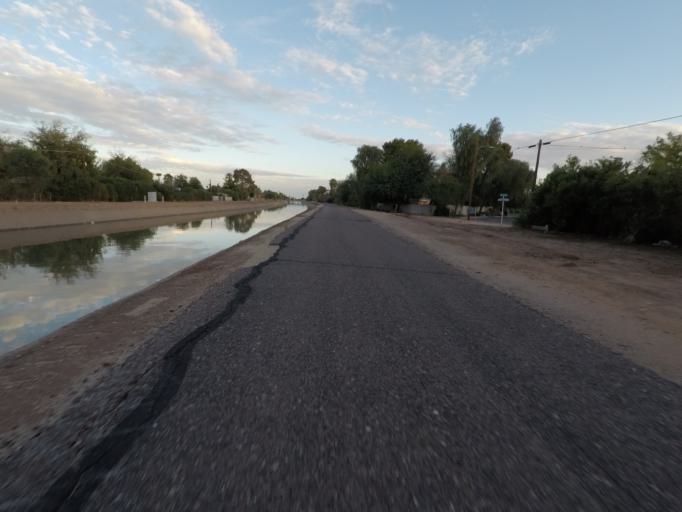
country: US
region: Arizona
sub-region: Maricopa County
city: Phoenix
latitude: 33.4752
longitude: -112.0282
